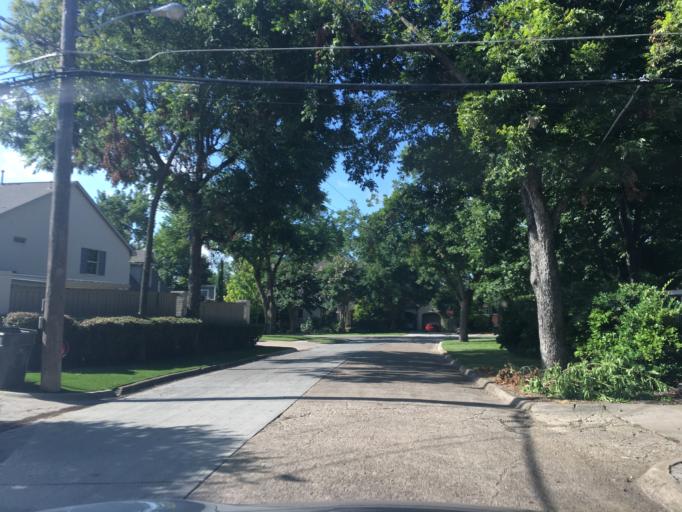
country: US
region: Texas
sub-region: Dallas County
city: Highland Park
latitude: 32.8320
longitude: -96.7469
